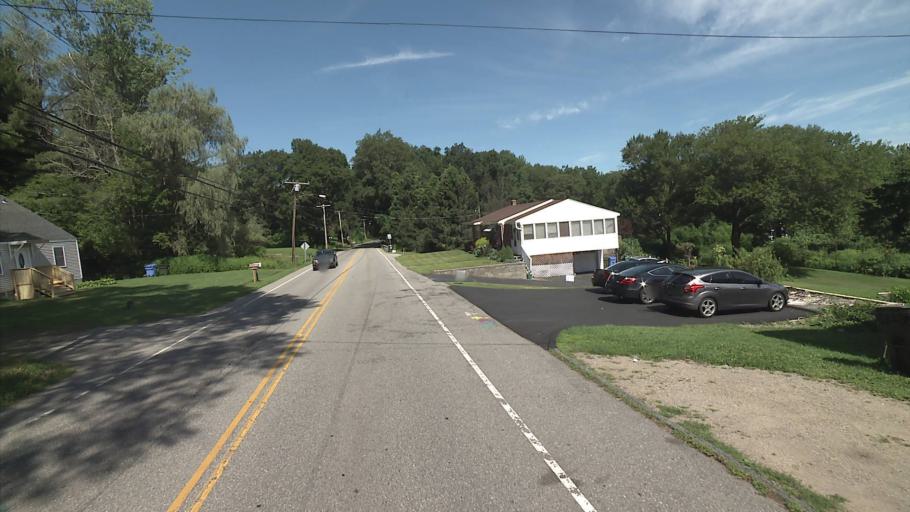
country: US
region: Connecticut
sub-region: New London County
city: Baltic
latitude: 41.5981
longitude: -72.0532
